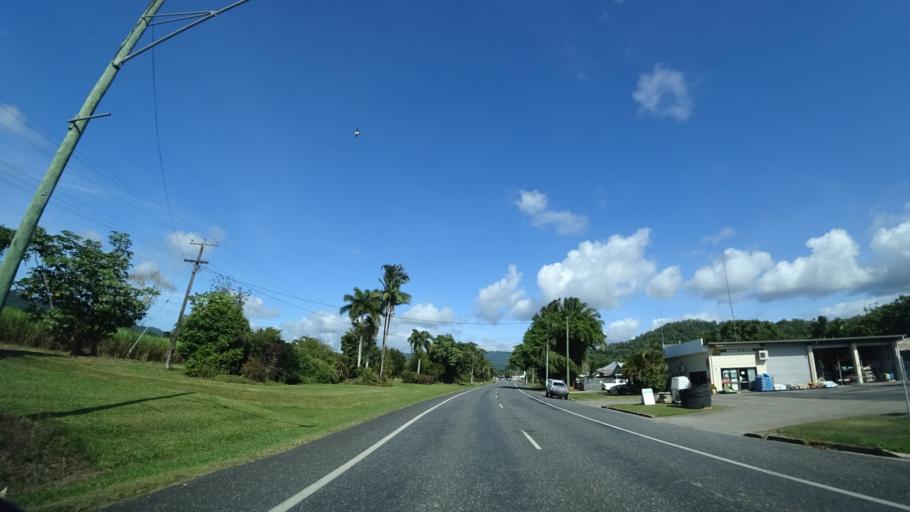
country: AU
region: Queensland
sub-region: Cairns
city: Port Douglas
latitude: -16.4797
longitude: 145.3767
